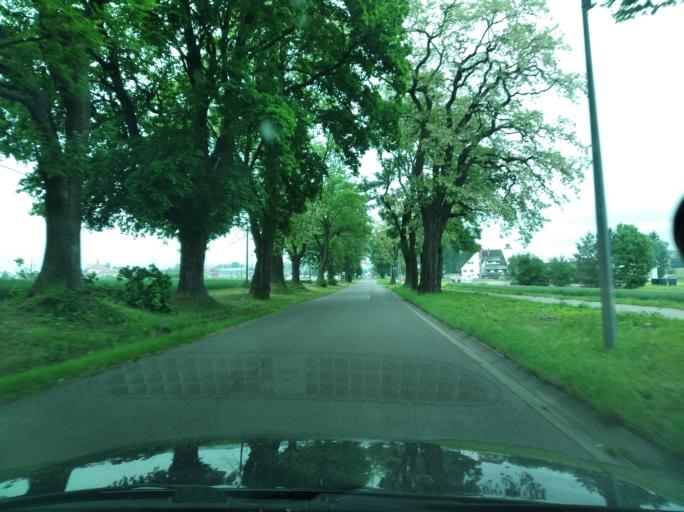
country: PL
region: Subcarpathian Voivodeship
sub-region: Powiat ropczycko-sedziszowski
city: Sedziszow Malopolski
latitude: 50.0605
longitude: 21.6895
